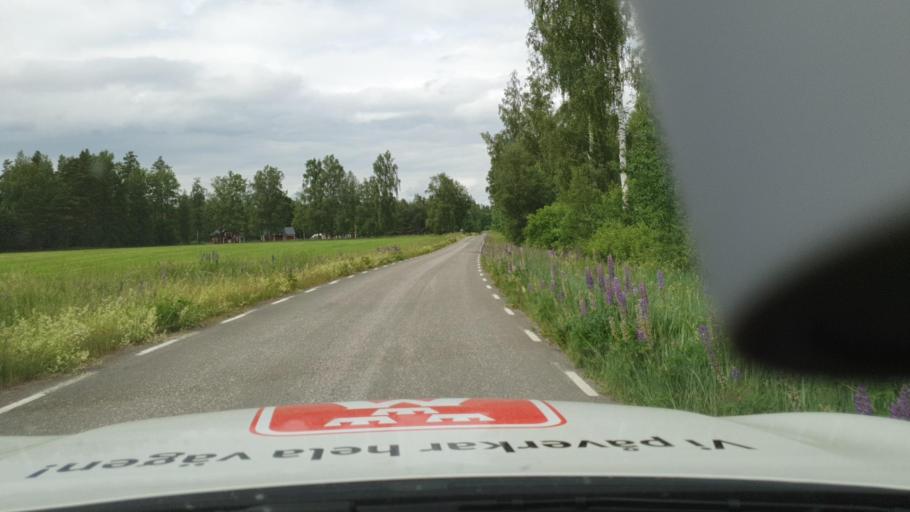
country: SE
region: Vaestra Goetaland
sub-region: Tidaholms Kommun
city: Tidaholm
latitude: 58.1666
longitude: 14.0151
